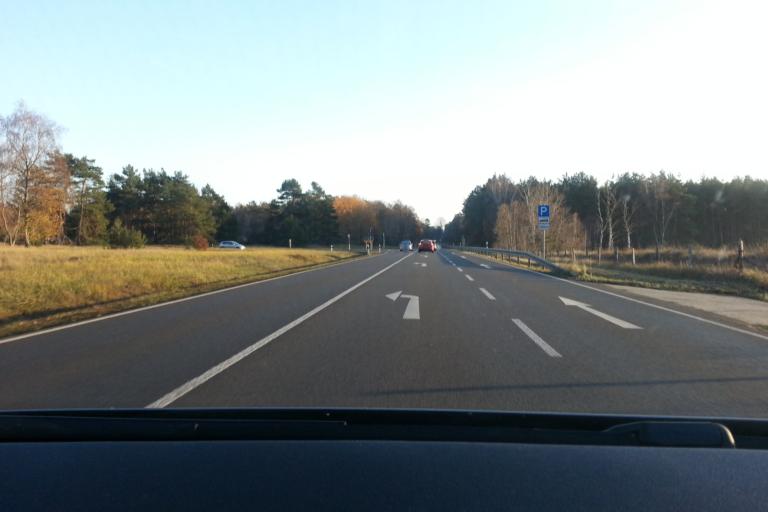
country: DE
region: Mecklenburg-Vorpommern
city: Ferdinandshof
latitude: 53.6437
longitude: 13.9144
